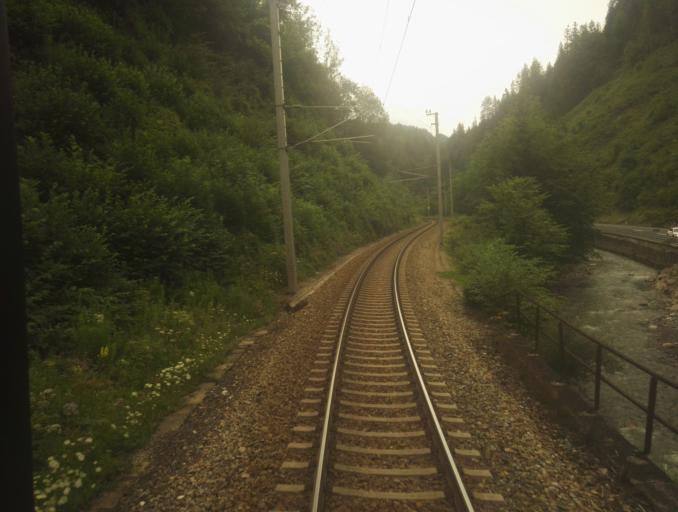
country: AT
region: Salzburg
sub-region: Politischer Bezirk Sankt Johann im Pongau
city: Huttau
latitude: 47.4296
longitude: 13.2661
